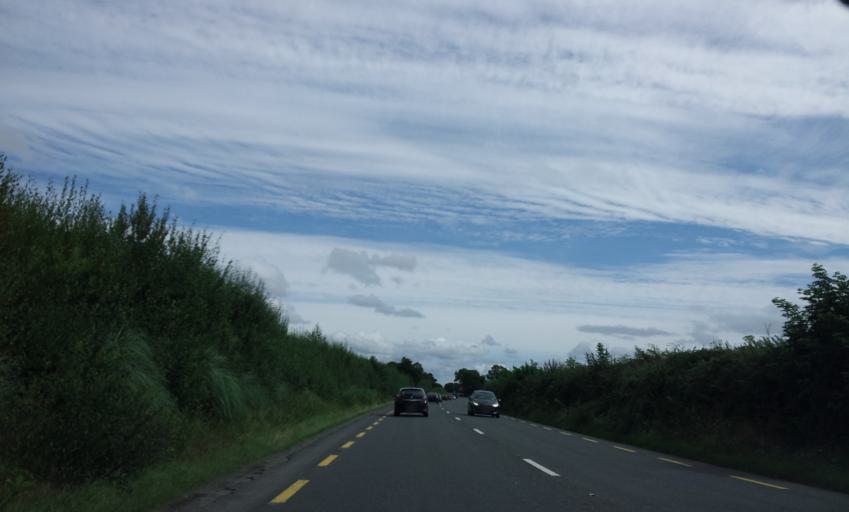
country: IE
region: Munster
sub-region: Ciarrai
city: Cill Airne
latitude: 52.0744
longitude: -9.6191
